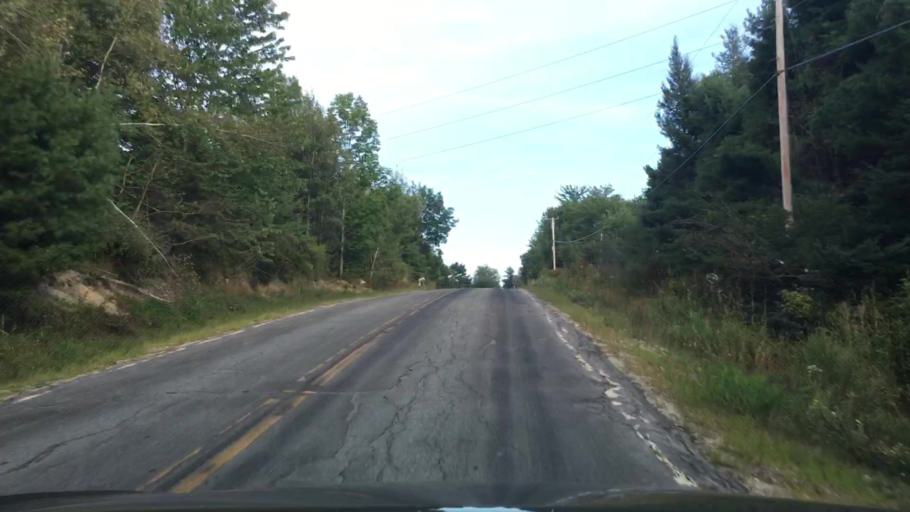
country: US
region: Maine
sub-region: Hancock County
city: Surry
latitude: 44.5057
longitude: -68.5912
